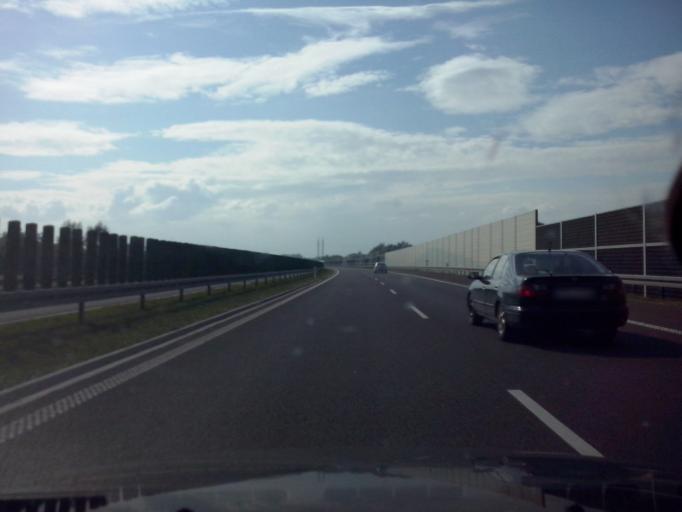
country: PL
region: Lesser Poland Voivodeship
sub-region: Powiat tarnowski
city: Lukowa
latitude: 50.0582
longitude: 20.9342
